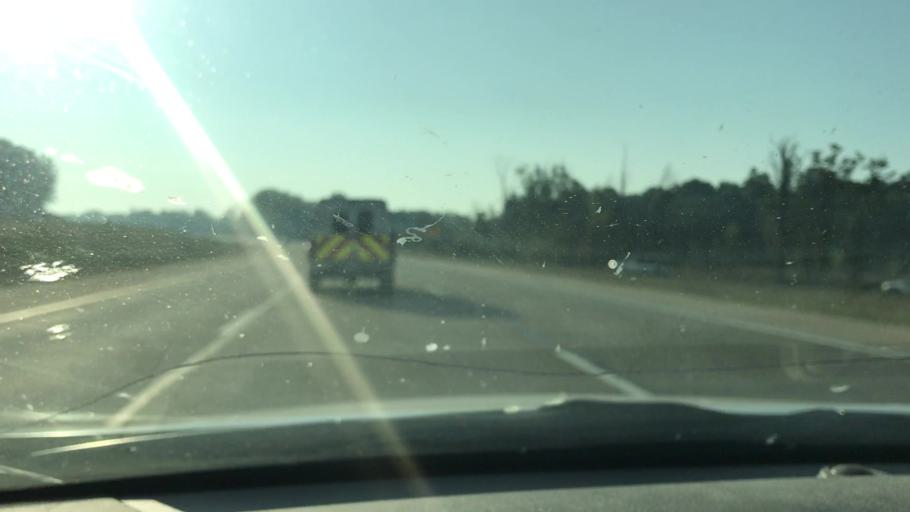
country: US
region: Michigan
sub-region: Livingston County
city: Howell
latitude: 42.6130
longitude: -83.9887
